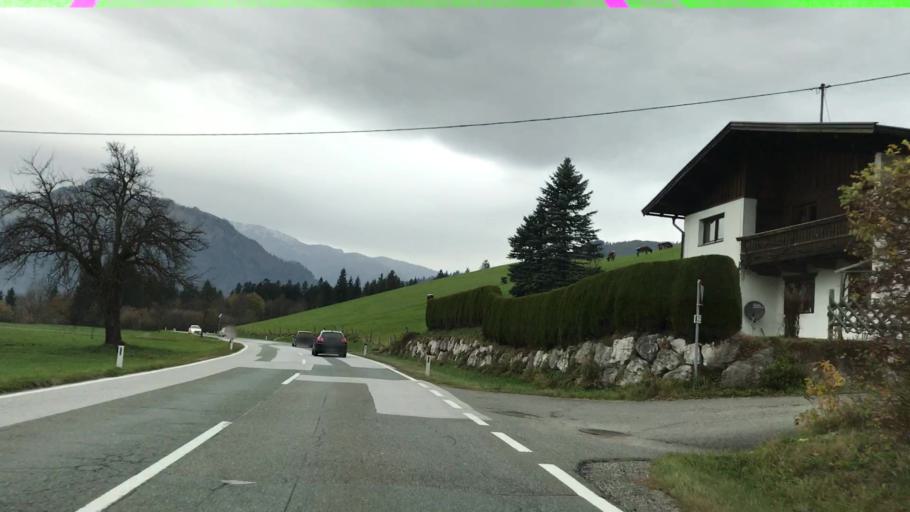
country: AT
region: Tyrol
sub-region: Politischer Bezirk Kitzbuhel
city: Kossen
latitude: 47.6560
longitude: 12.4289
